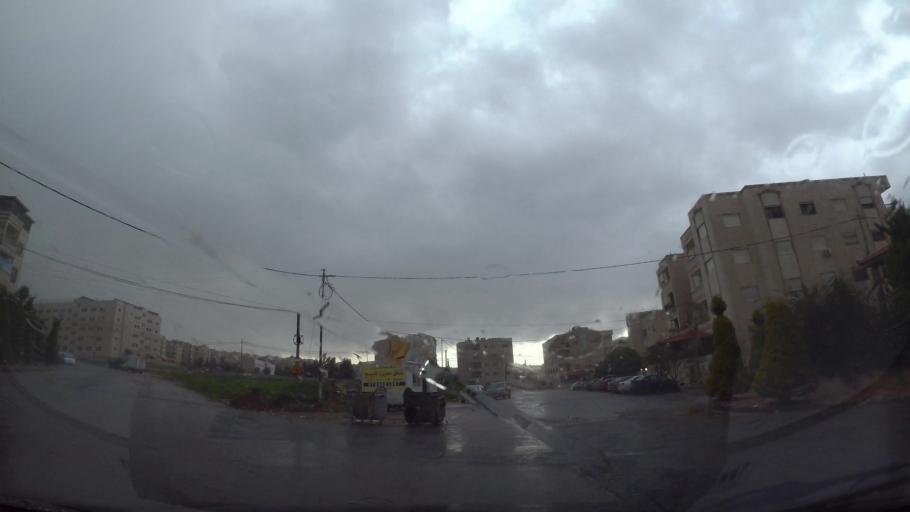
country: JO
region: Amman
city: Amman
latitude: 32.0045
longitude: 35.9566
